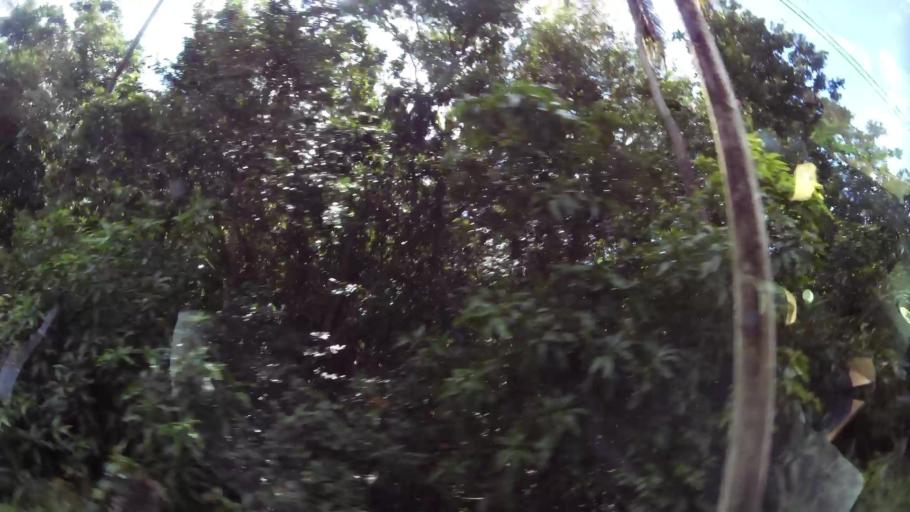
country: DM
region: Saint John
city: Portsmouth
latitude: 15.6060
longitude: -61.4628
